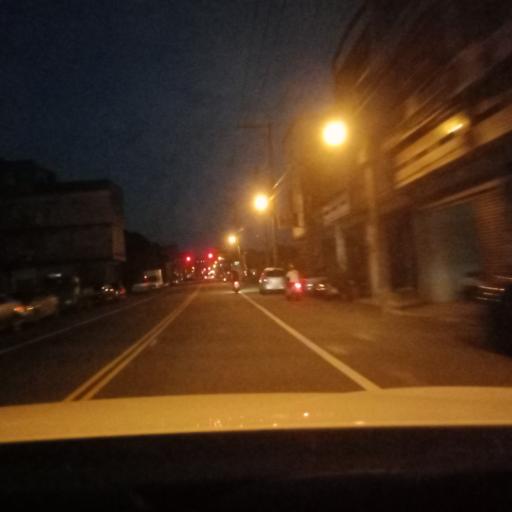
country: TW
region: Taiwan
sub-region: Hsinchu
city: Zhubei
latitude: 24.9124
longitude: 121.0508
